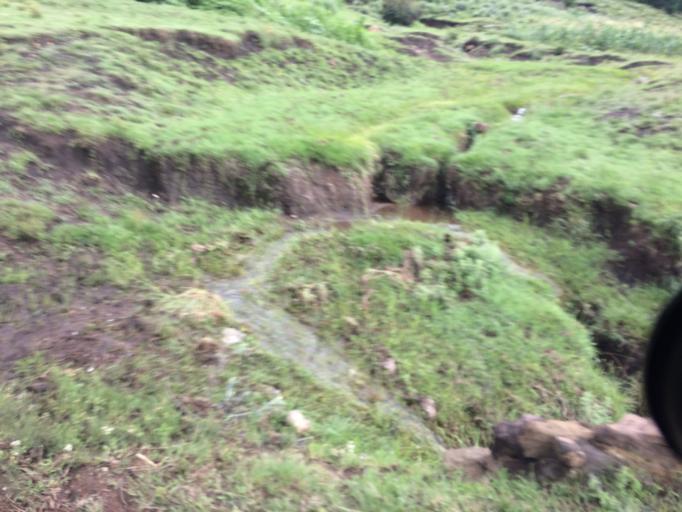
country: LS
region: Maseru
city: Nako
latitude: -29.8448
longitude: 27.5609
